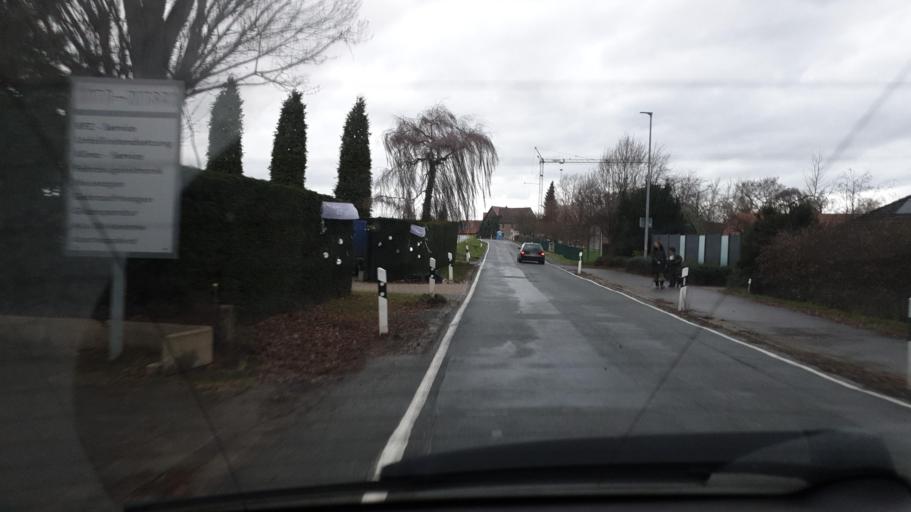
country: DE
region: North Rhine-Westphalia
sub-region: Regierungsbezirk Detmold
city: Lemgo
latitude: 52.0742
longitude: 8.8636
